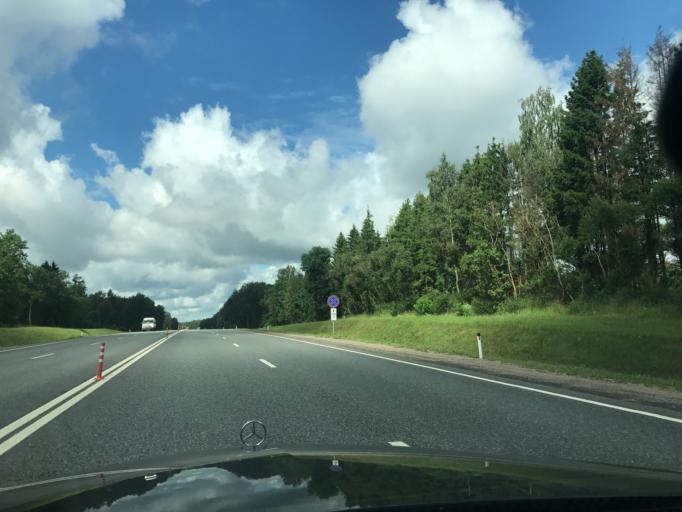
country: RU
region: Smolensk
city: Golynki
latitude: 54.7407
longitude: 31.3905
